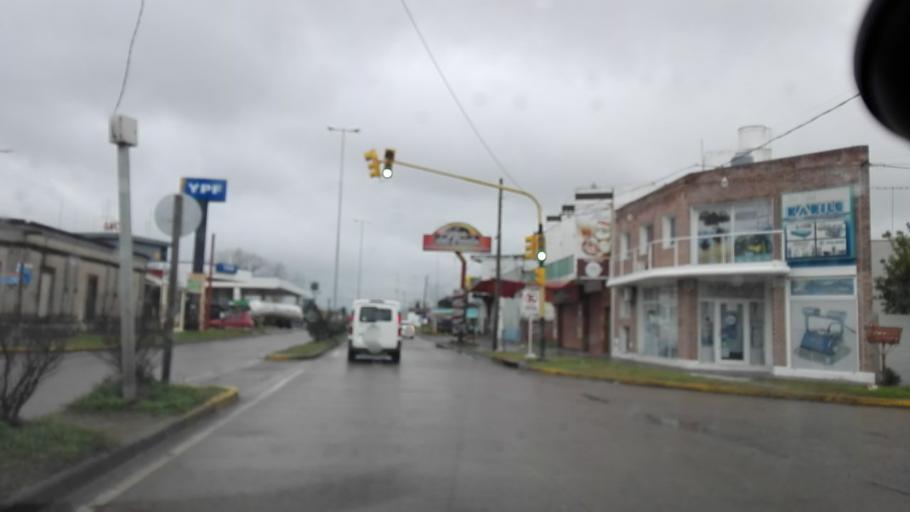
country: AR
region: Buenos Aires
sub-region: Partido de Brandsen
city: Brandsen
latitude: -35.1725
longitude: -58.2313
